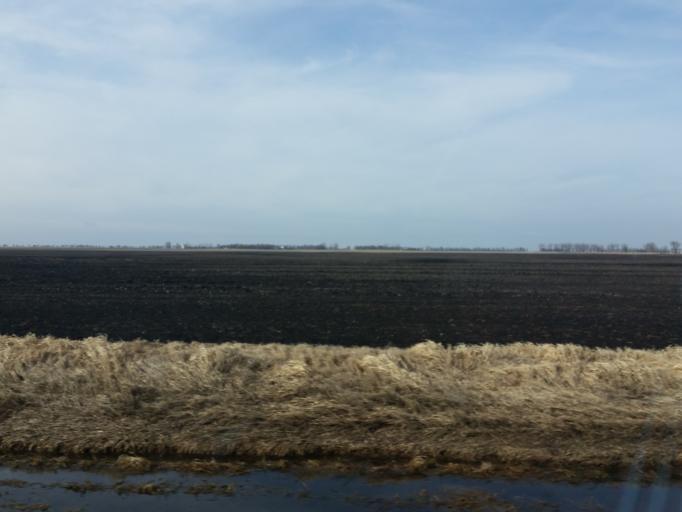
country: US
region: North Dakota
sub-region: Richland County
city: Wahpeton
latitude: 46.4711
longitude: -96.6285
